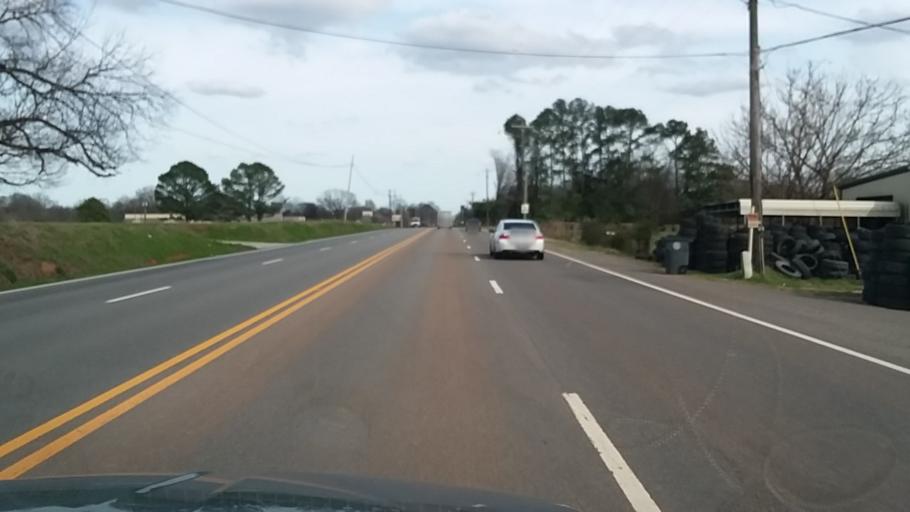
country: US
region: Alabama
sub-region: Lawrence County
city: Town Creek
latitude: 34.6815
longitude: -87.4209
